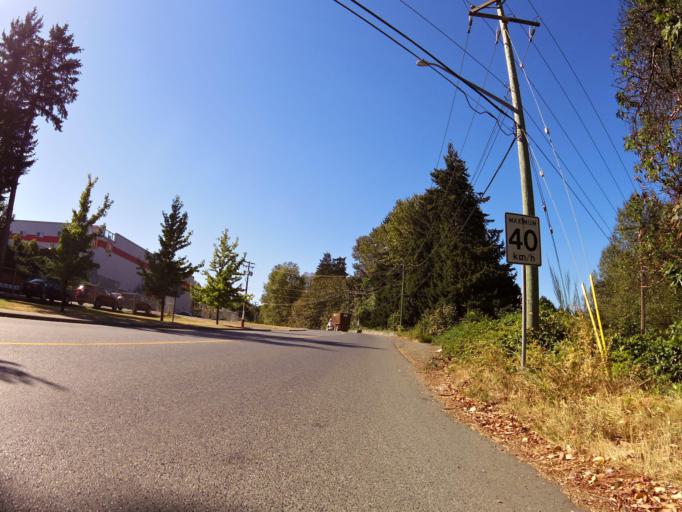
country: CA
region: British Columbia
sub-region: Cowichan Valley Regional District
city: Ladysmith
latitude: 48.9998
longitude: -123.8223
